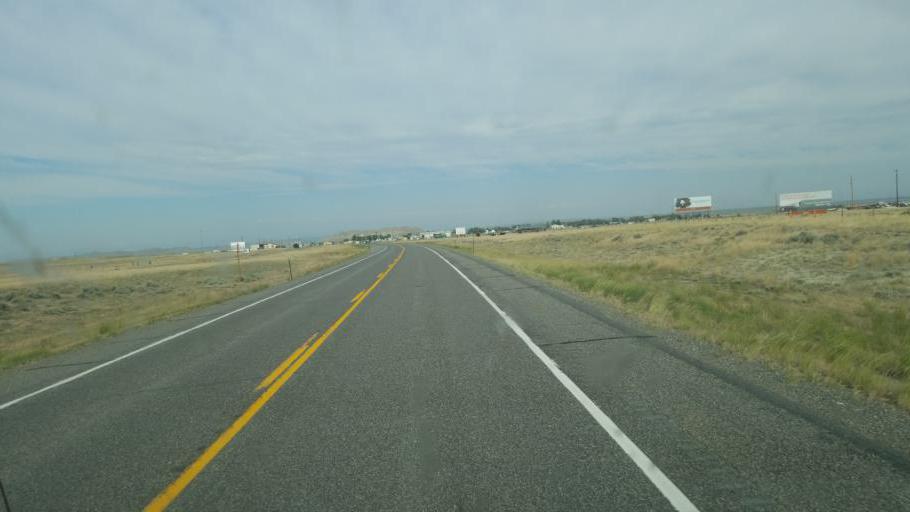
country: US
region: Wyoming
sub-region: Fremont County
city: Riverton
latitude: 43.2369
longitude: -108.0896
